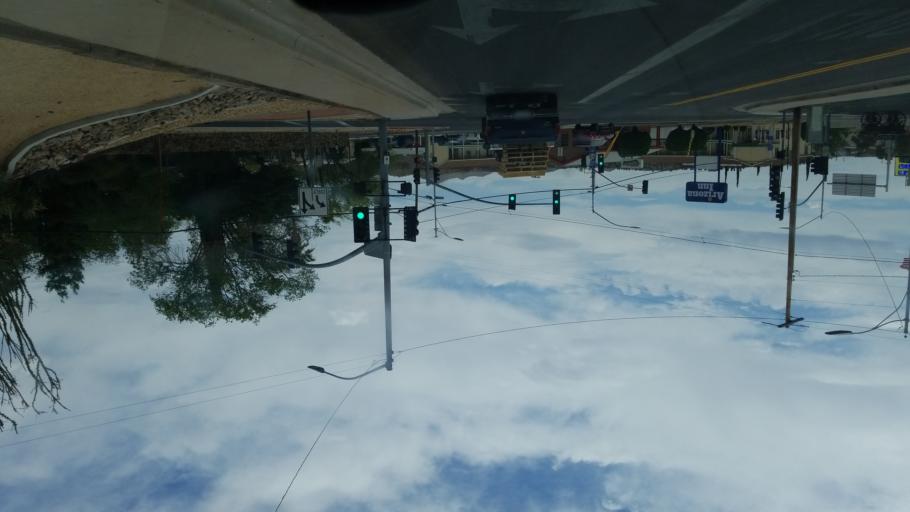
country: US
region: Arizona
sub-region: Mohave County
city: Kingman
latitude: 35.1900
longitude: -114.0609
